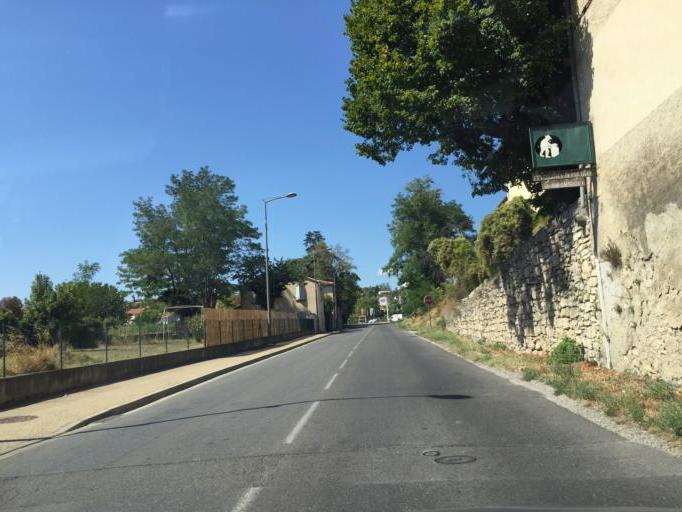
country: FR
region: Provence-Alpes-Cote d'Azur
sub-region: Departement des Alpes-de-Haute-Provence
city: Forcalquier
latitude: 43.9597
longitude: 5.7860
